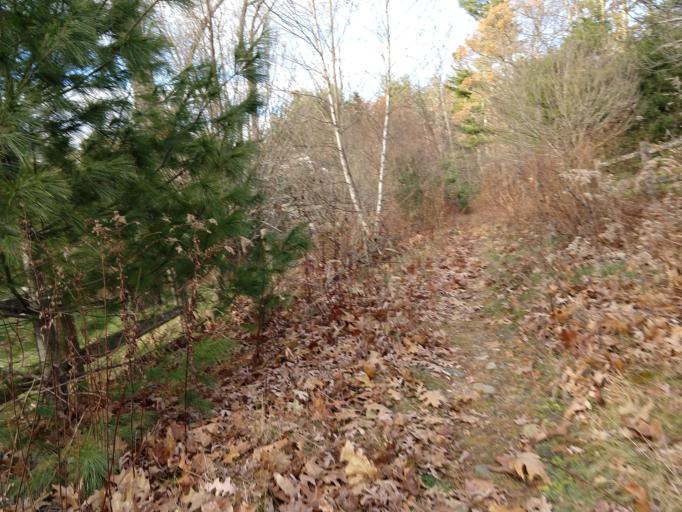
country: US
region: Massachusetts
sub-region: Middlesex County
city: Westford
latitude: 42.5464
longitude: -71.4328
